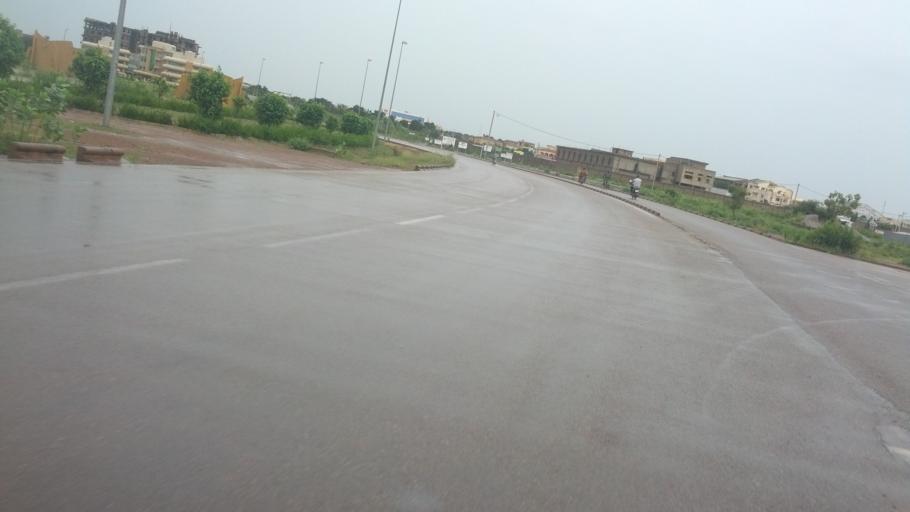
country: BF
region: Centre
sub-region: Kadiogo Province
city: Ouagadougou
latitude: 12.3137
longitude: -1.5047
